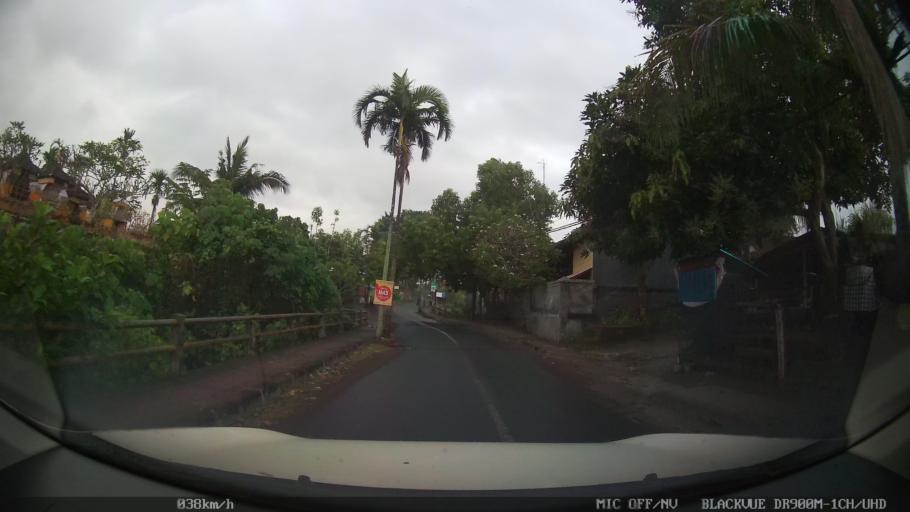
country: ID
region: Bali
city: Banjar Desa
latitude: -8.5857
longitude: 115.2790
